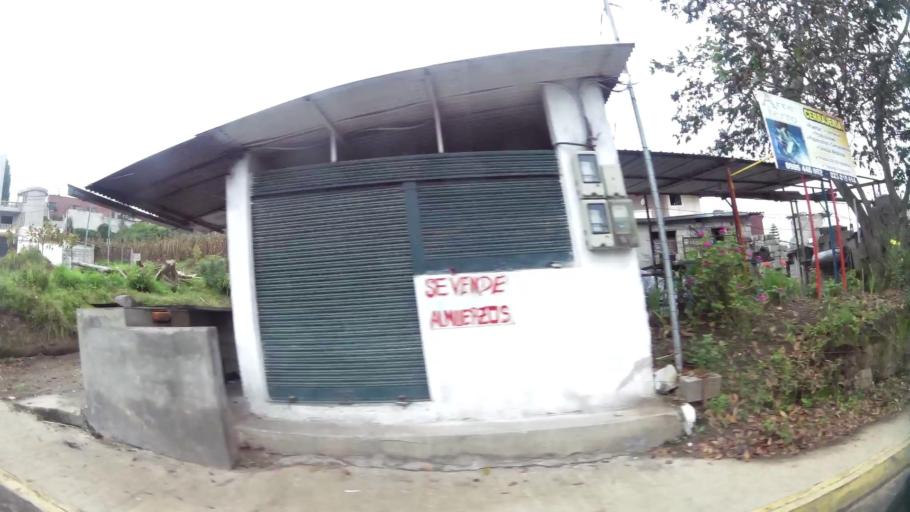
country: EC
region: Pichincha
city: Quito
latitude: -0.2628
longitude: -78.4838
